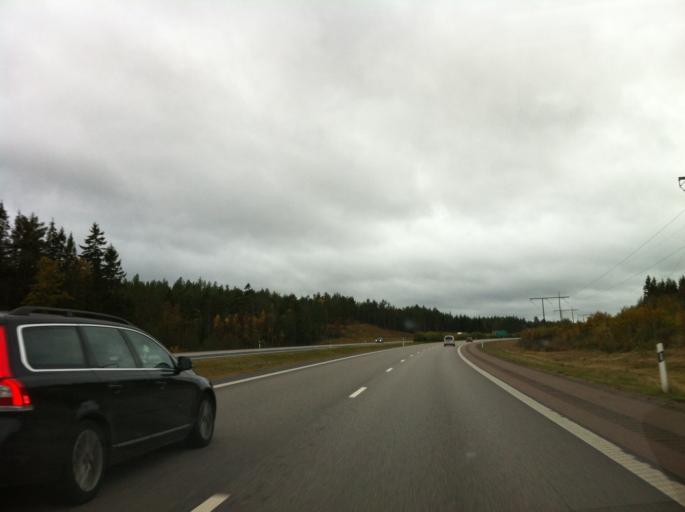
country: SE
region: OEstergoetland
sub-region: Vadstena Kommun
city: Herrestad
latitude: 58.2685
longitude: 14.8590
